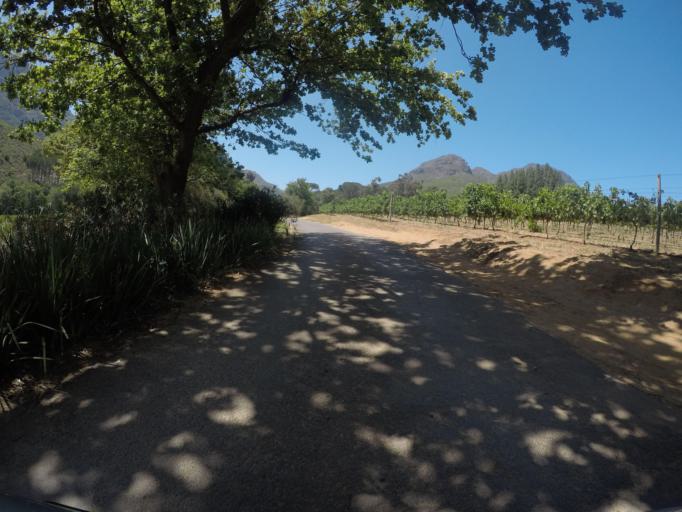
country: ZA
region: Western Cape
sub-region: Cape Winelands District Municipality
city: Stellenbosch
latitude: -34.0030
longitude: 18.8873
